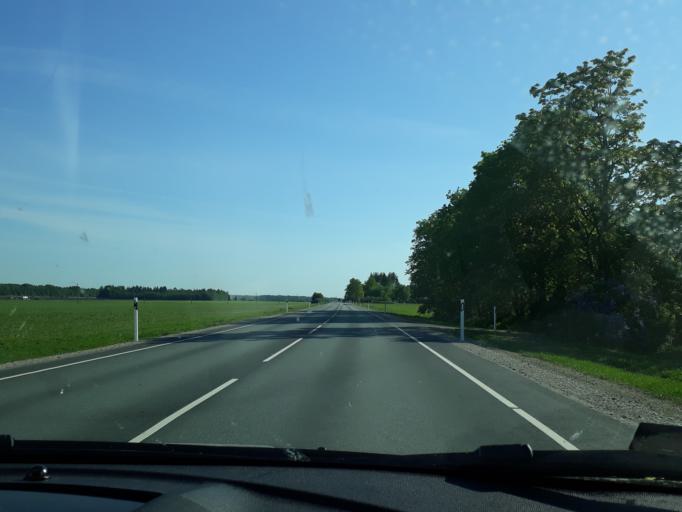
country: EE
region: Paernumaa
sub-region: Tootsi vald
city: Tootsi
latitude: 58.5494
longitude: 24.8492
